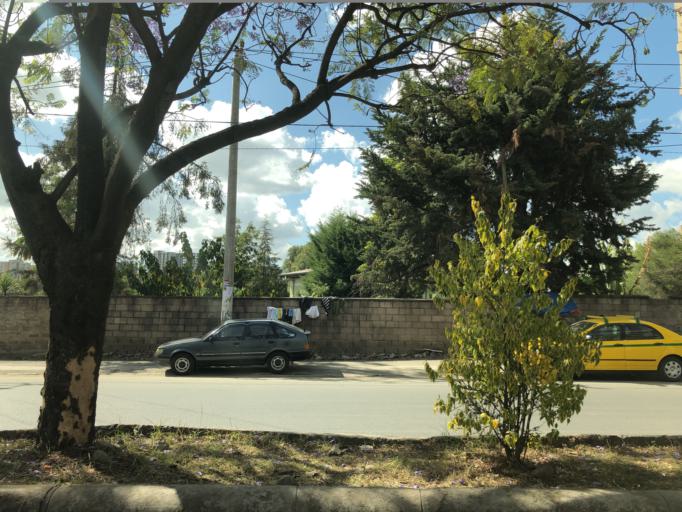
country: ET
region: Adis Abeba
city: Addis Ababa
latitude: 8.9975
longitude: 38.7791
